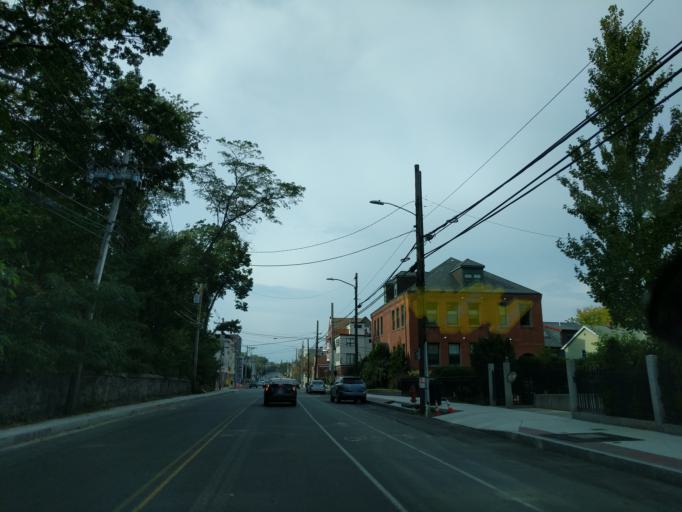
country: US
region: Massachusetts
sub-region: Middlesex County
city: Cambridge
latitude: 42.3814
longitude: -71.1102
